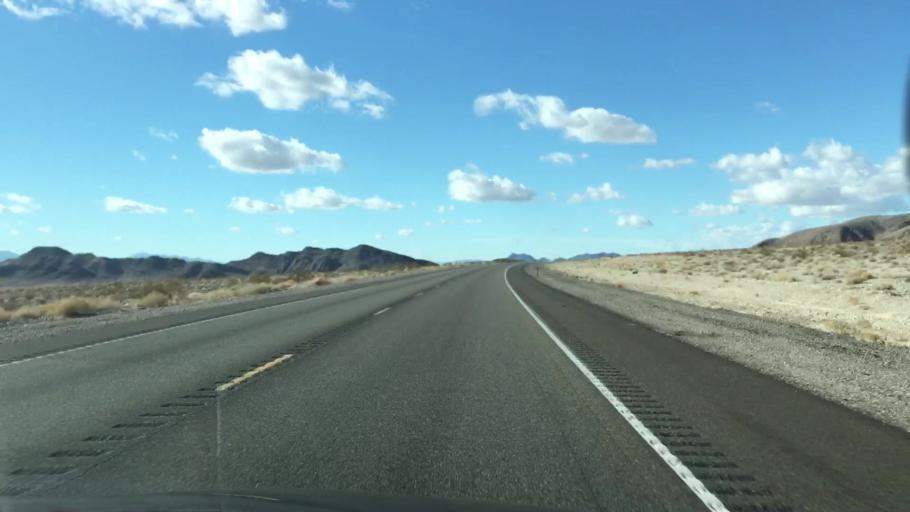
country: US
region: Nevada
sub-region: Nye County
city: Pahrump
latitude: 36.5733
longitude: -116.1829
